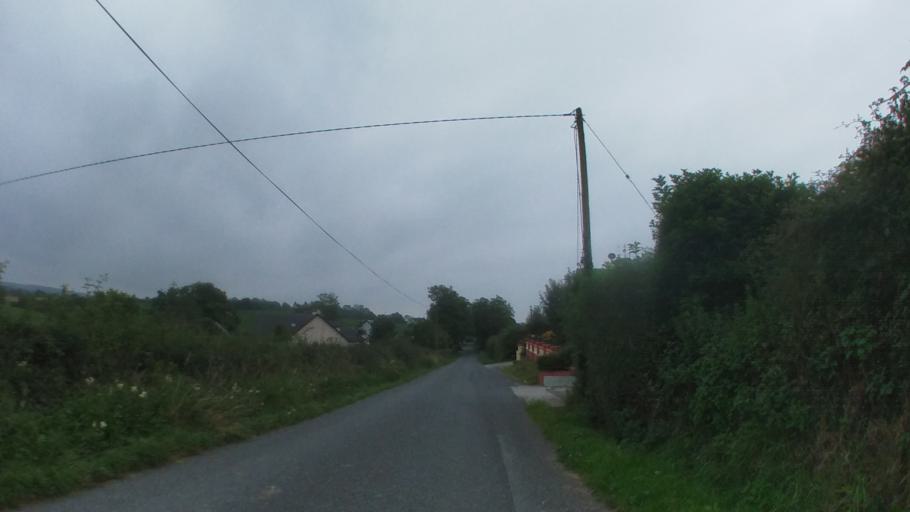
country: IE
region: Leinster
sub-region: Kilkenny
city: Kilkenny
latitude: 52.7056
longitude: -7.1929
